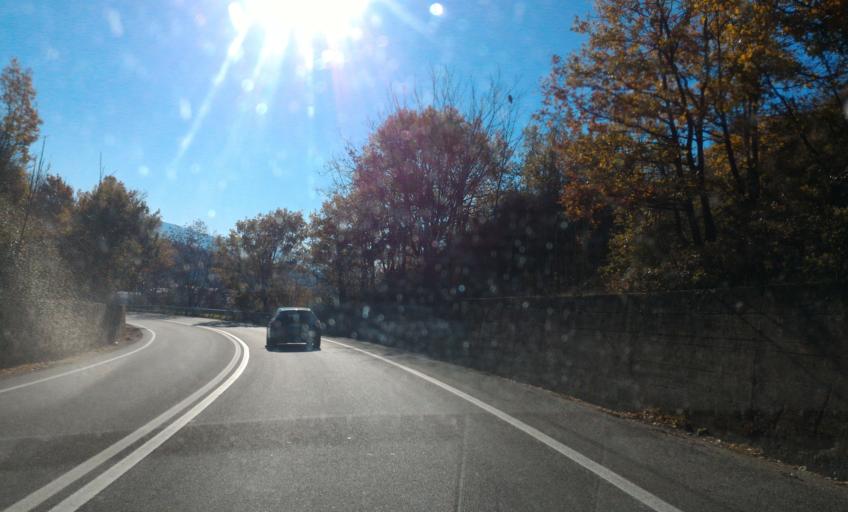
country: IT
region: Calabria
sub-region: Provincia di Cosenza
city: Rovito
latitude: 39.3048
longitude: 16.3094
